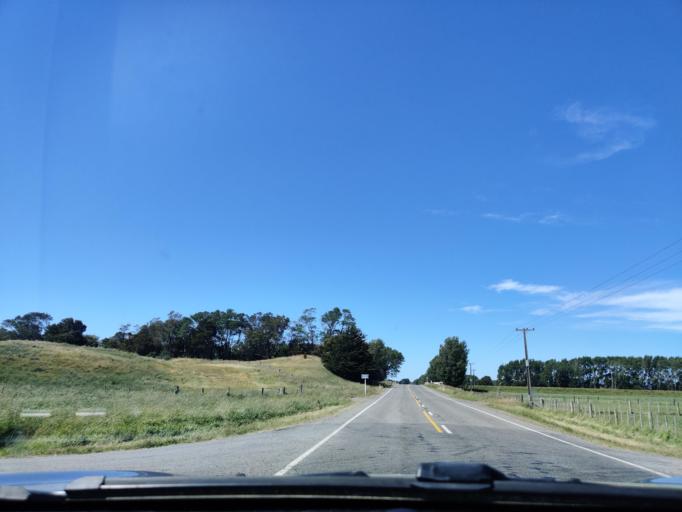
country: NZ
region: Wellington
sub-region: Upper Hutt City
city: Upper Hutt
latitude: -41.2640
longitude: 175.2785
